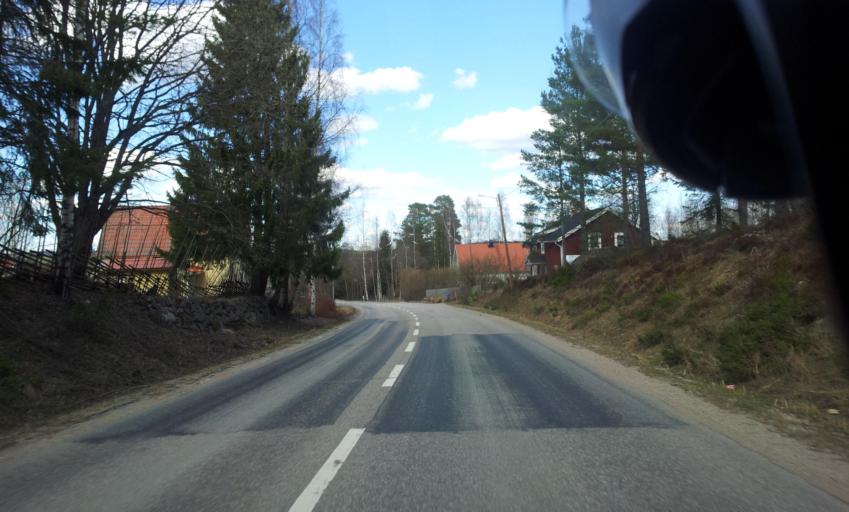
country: SE
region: Gaevleborg
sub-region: Ovanakers Kommun
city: Edsbyn
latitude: 61.3621
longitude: 15.8146
